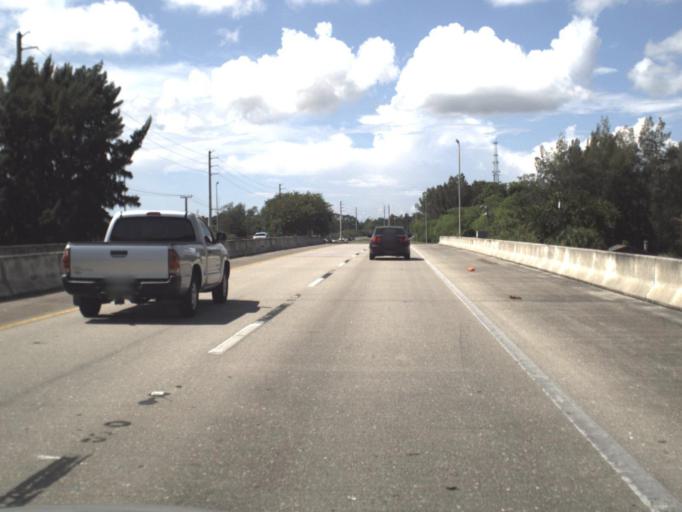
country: US
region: Florida
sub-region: Sarasota County
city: Warm Mineral Springs
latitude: 27.0455
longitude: -82.2927
